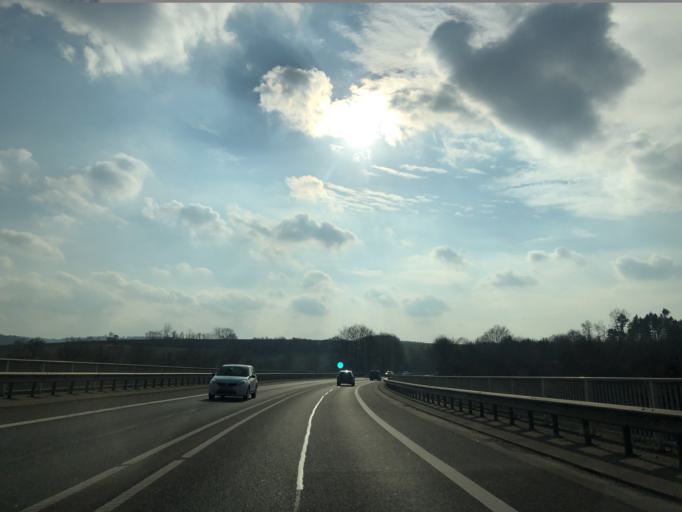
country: DE
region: Rheinland-Pfalz
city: Holler
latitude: 50.4324
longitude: 7.8423
